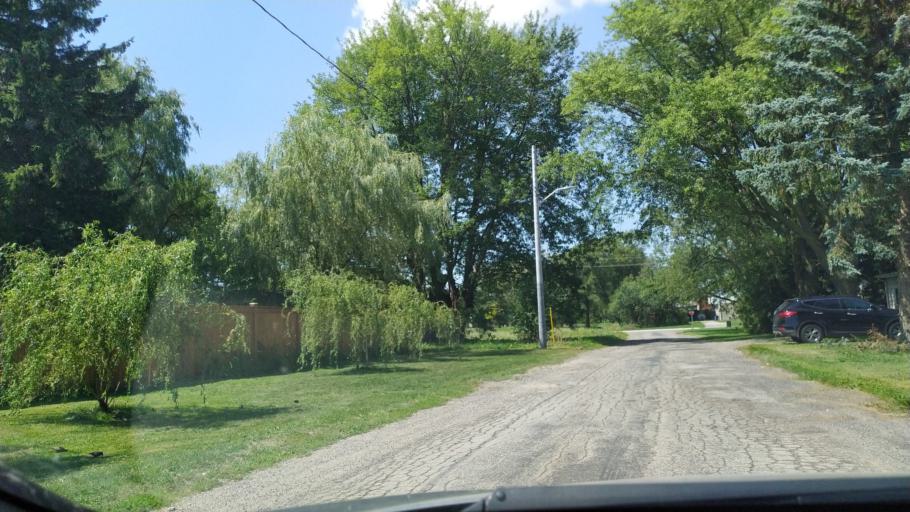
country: CA
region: Ontario
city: Stratford
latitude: 43.3589
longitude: -80.9997
